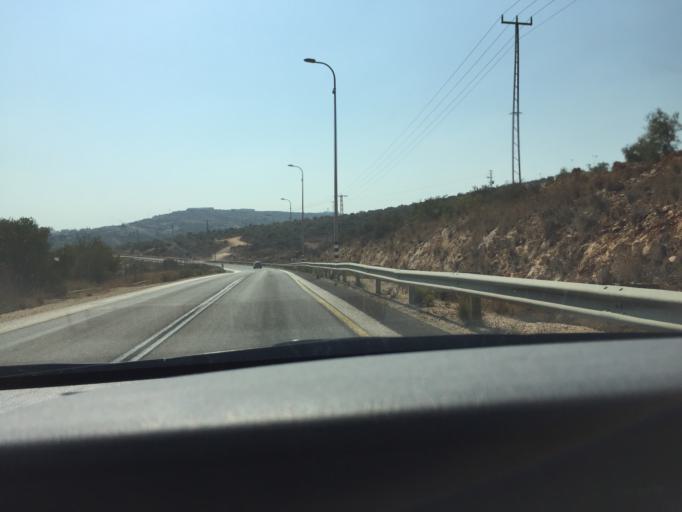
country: PS
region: West Bank
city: Bruqin
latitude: 32.0779
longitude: 35.0901
